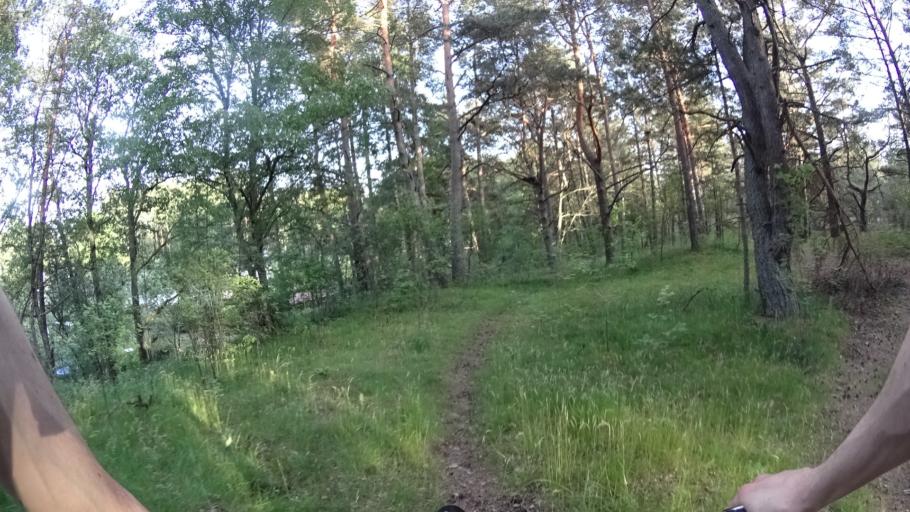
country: LV
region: Riga
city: Jaunciems
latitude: 57.1068
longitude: 24.1927
